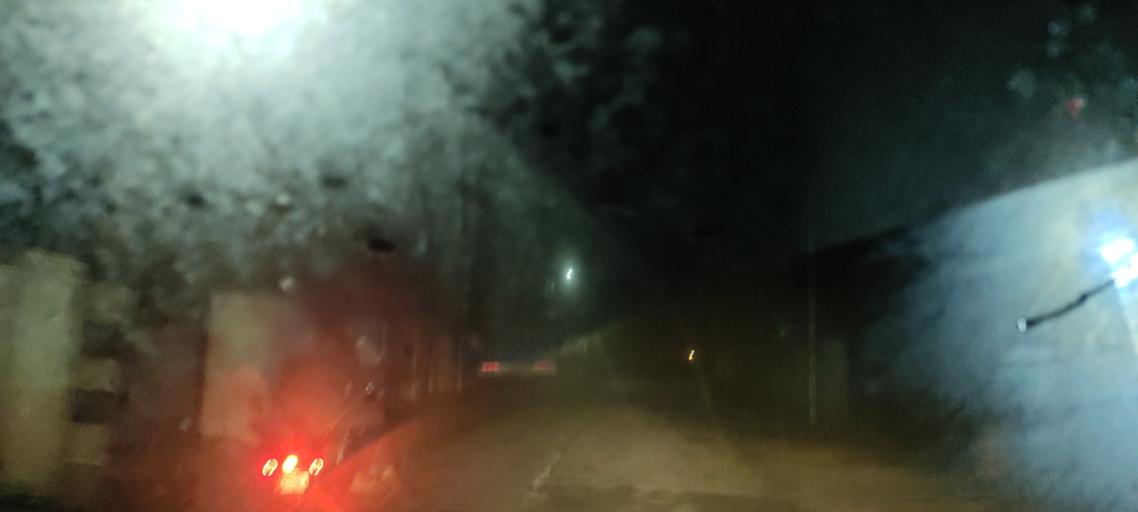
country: IN
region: Kerala
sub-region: Alappuzha
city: Vayalar
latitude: 9.7230
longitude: 76.3363
